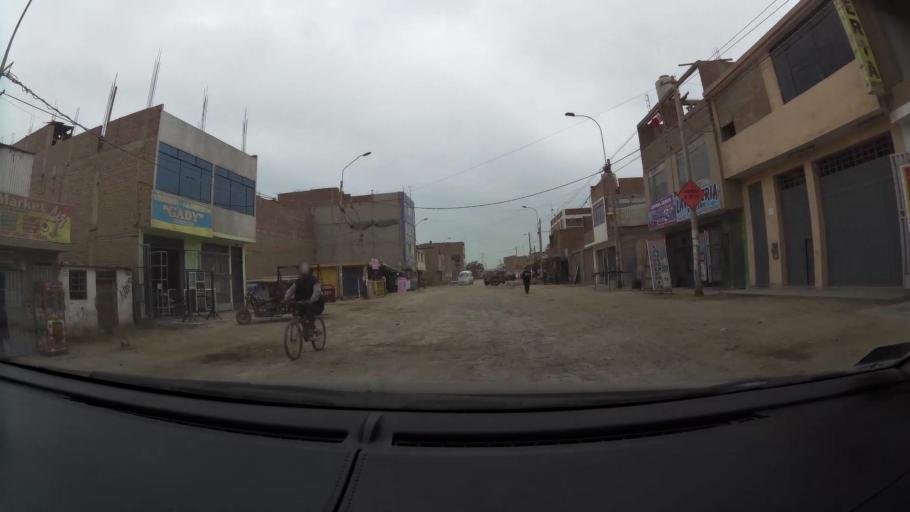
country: PE
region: Lima
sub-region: Lima
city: Independencia
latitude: -11.9588
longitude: -77.0975
